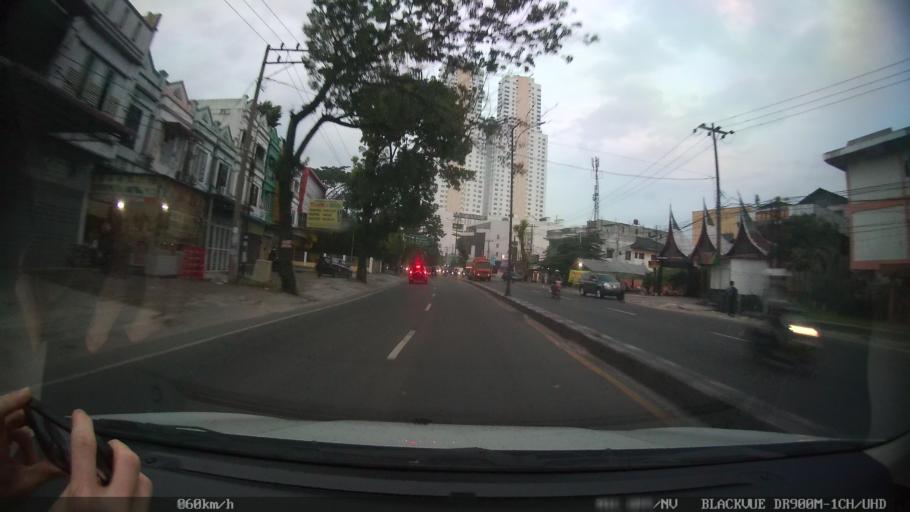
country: ID
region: North Sumatra
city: Sunggal
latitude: 3.5920
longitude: 98.6236
